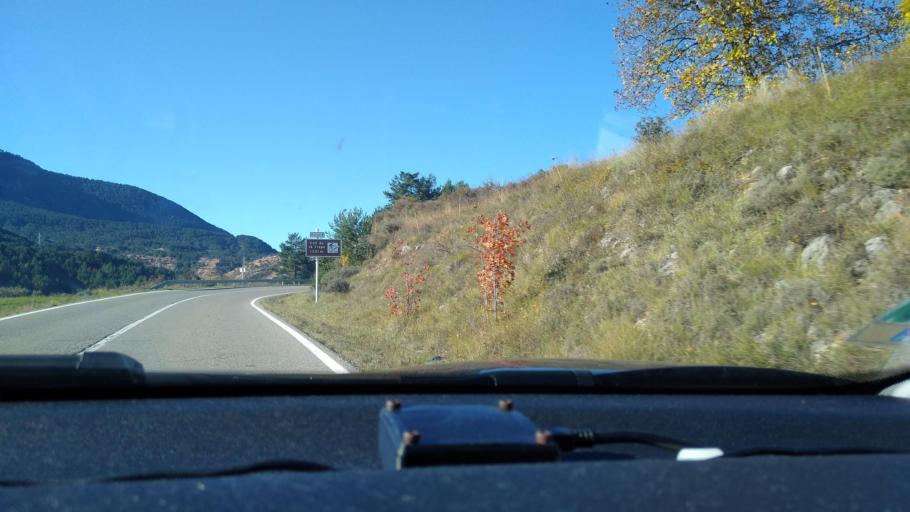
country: ES
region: Catalonia
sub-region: Provincia de Barcelona
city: Saldes
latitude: 42.2255
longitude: 1.7335
